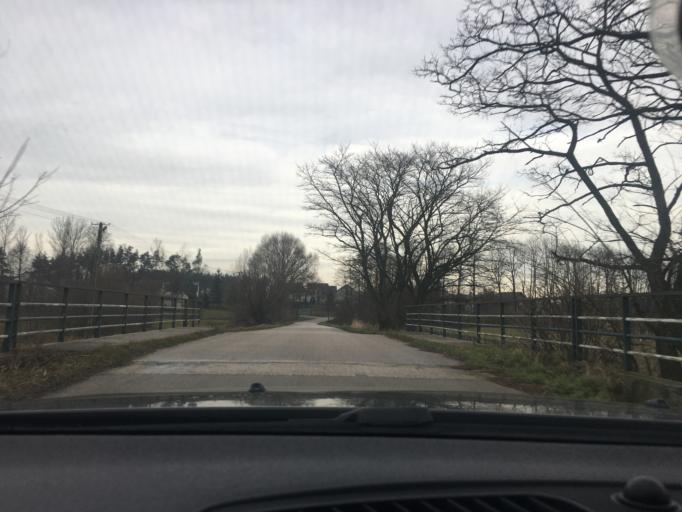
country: PL
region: Swietokrzyskie
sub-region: Powiat jedrzejowski
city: Imielno
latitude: 50.6390
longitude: 20.4155
